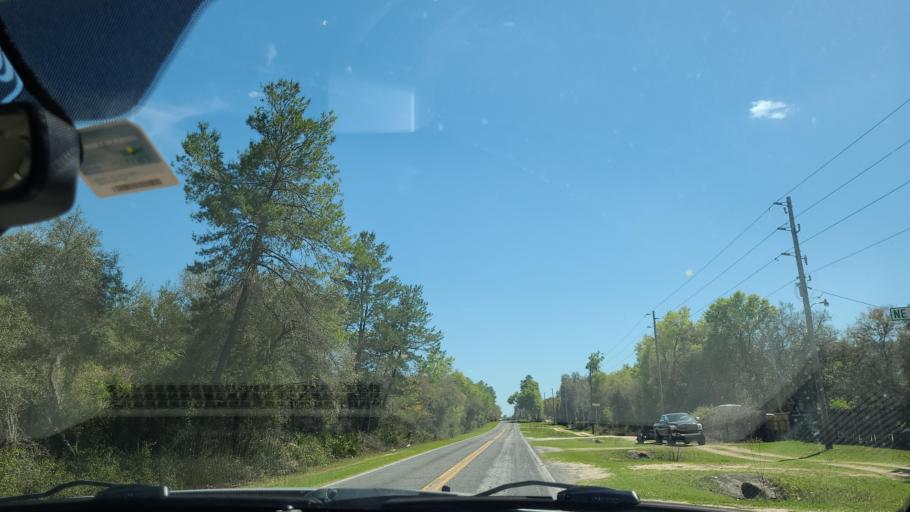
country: US
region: Florida
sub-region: Marion County
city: Citra
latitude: 29.4279
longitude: -81.9152
